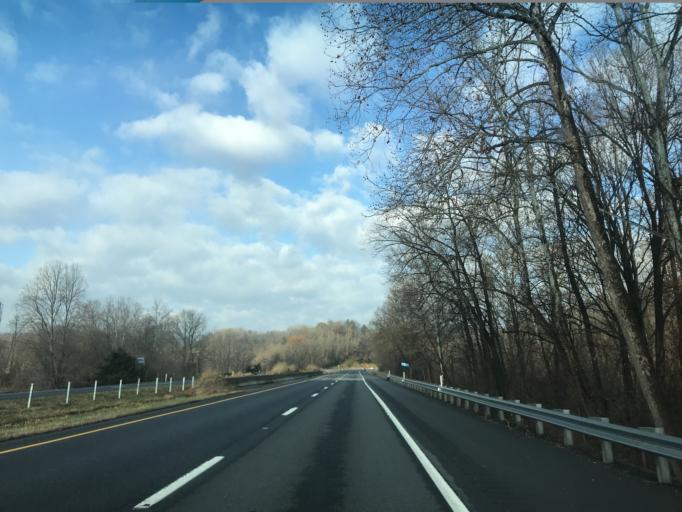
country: US
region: Maryland
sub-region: Washington County
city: Hancock
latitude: 39.7618
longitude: -78.1956
